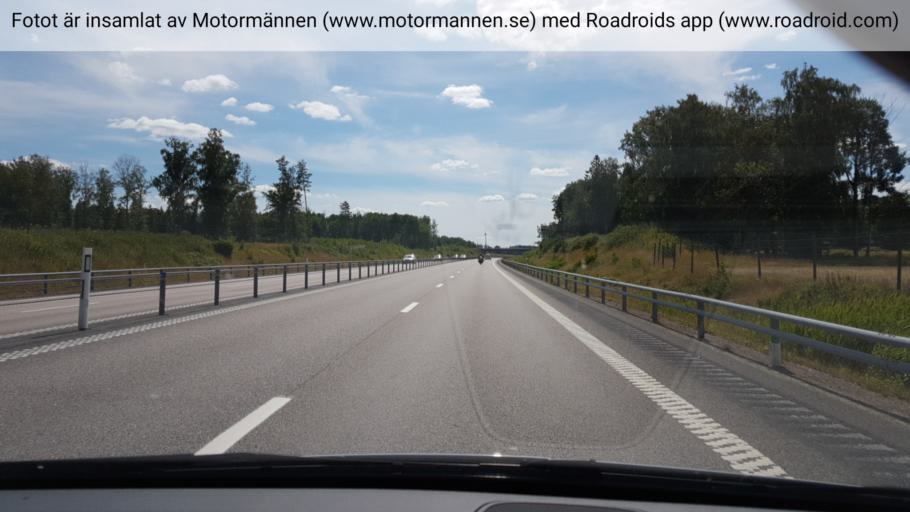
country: SE
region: Vaestra Goetaland
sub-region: Gotene Kommun
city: Goetene
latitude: 58.5108
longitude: 13.5077
